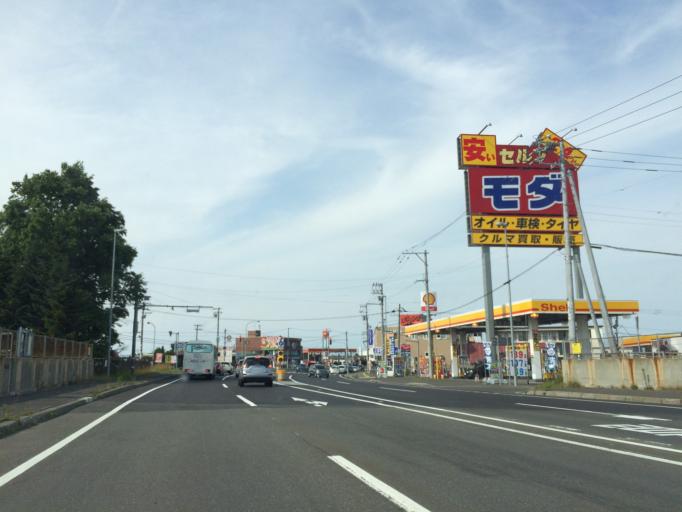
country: JP
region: Hokkaido
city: Ebetsu
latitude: 43.0865
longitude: 141.5156
